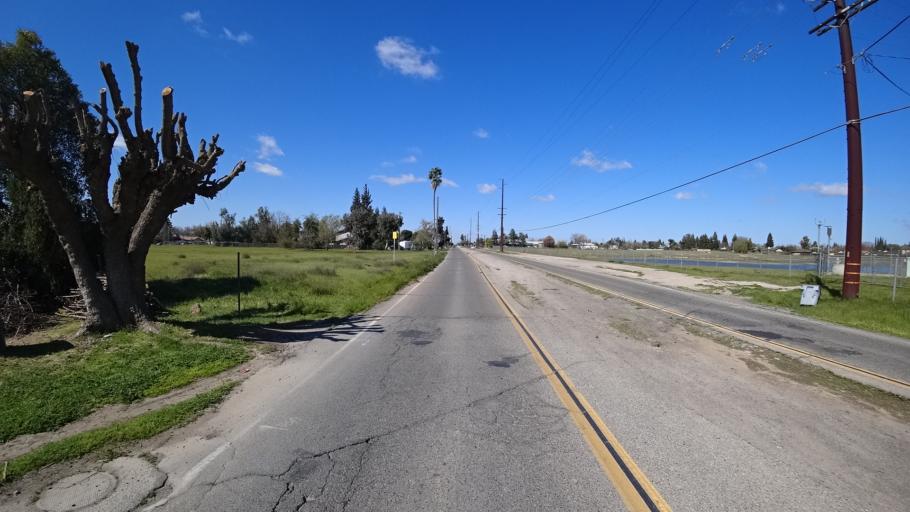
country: US
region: California
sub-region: Fresno County
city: West Park
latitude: 36.7935
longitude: -119.8849
